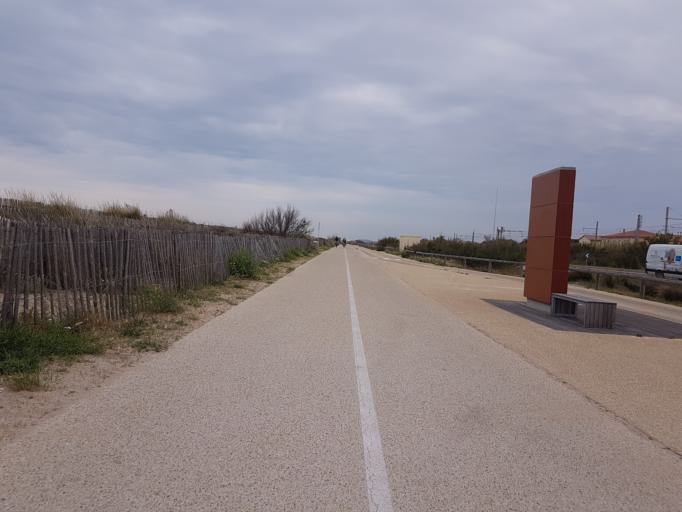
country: FR
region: Languedoc-Roussillon
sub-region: Departement de l'Herault
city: Meze
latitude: 43.3782
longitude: 3.6331
